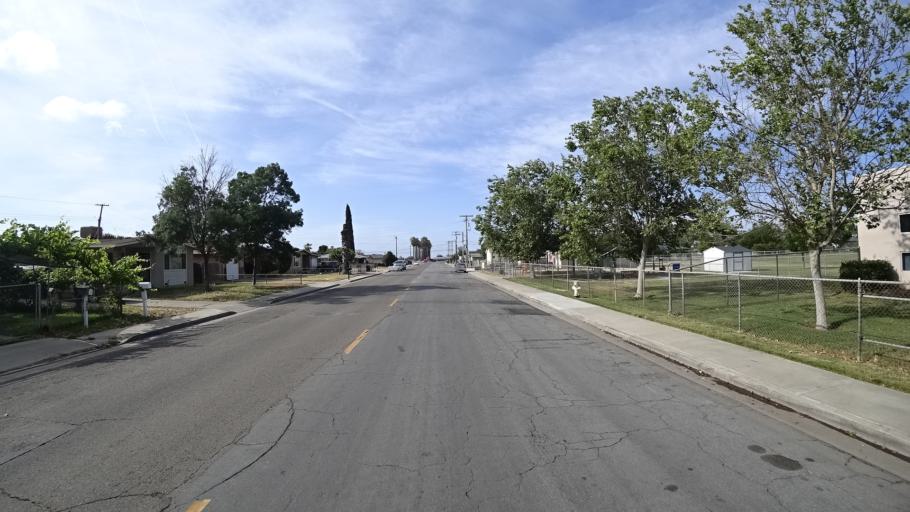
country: US
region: California
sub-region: Kings County
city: Hanford
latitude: 36.3154
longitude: -119.6426
